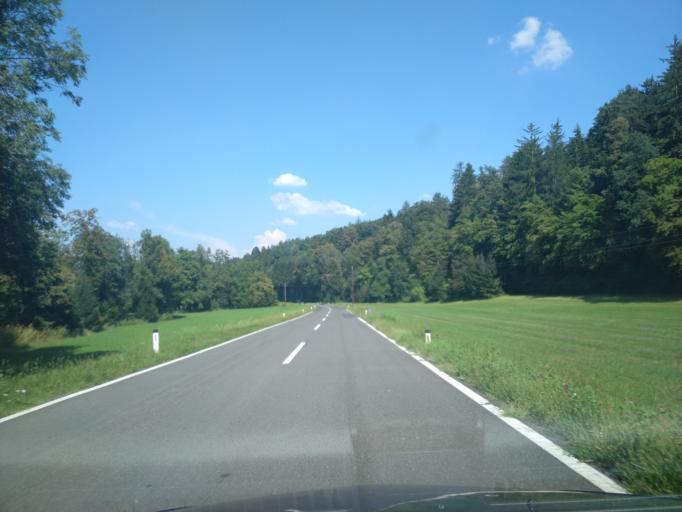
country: AT
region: Styria
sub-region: Politischer Bezirk Leibnitz
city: Leutschach
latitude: 46.7008
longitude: 15.5010
